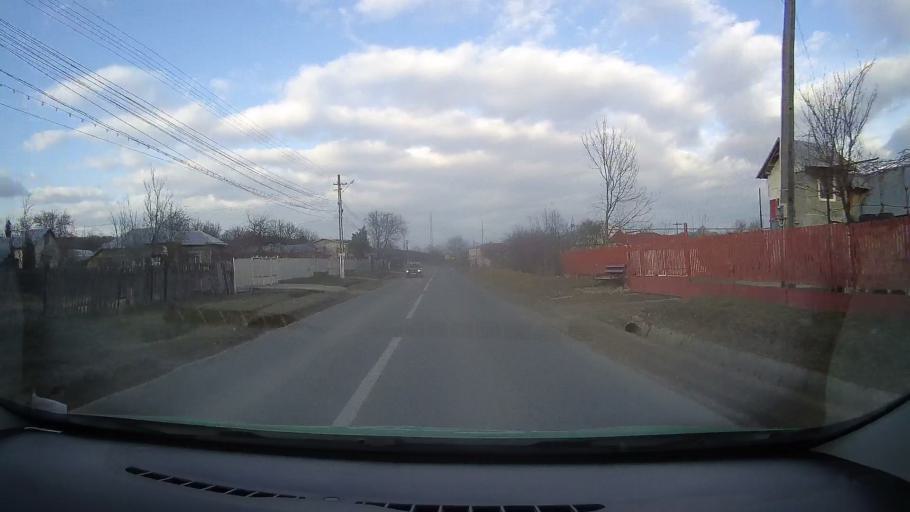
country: RO
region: Dambovita
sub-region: Comuna Gura Ocnitei
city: Gura Ocnitei
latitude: 44.9396
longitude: 25.5796
